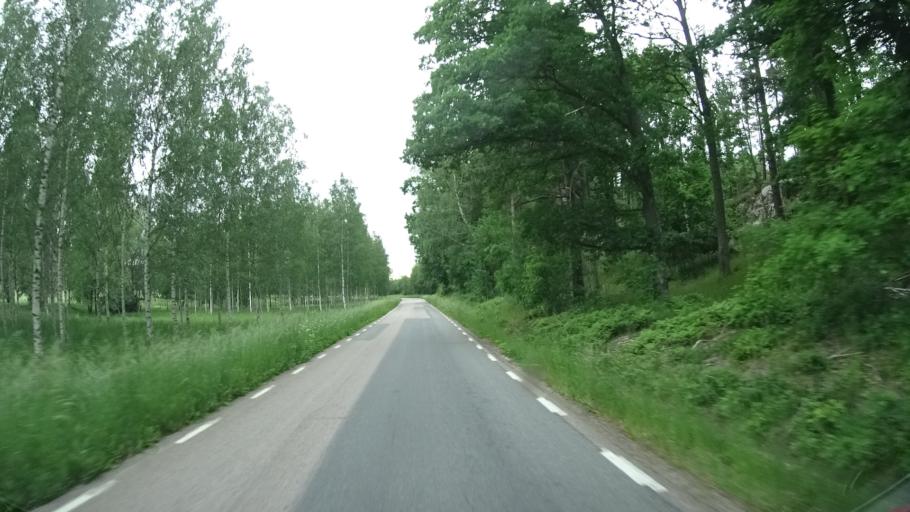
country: SE
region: Soedermanland
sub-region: Nykopings Kommun
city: Stigtomta
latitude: 58.7553
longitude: 16.7201
